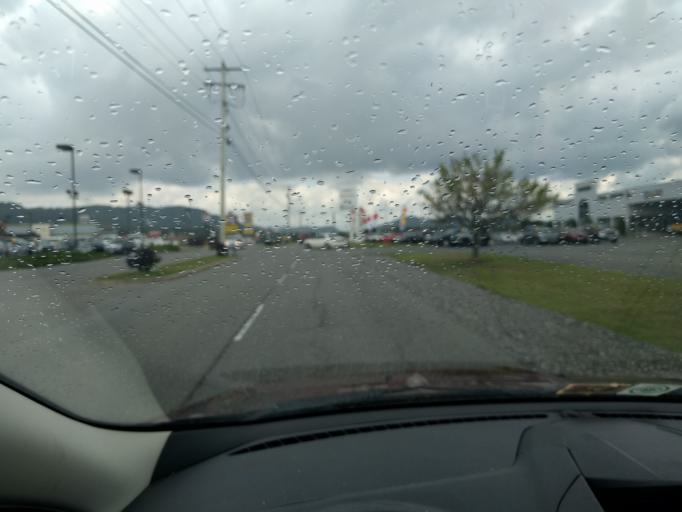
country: US
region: West Virginia
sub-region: Nicholas County
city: Summersville
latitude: 38.3037
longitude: -80.8320
